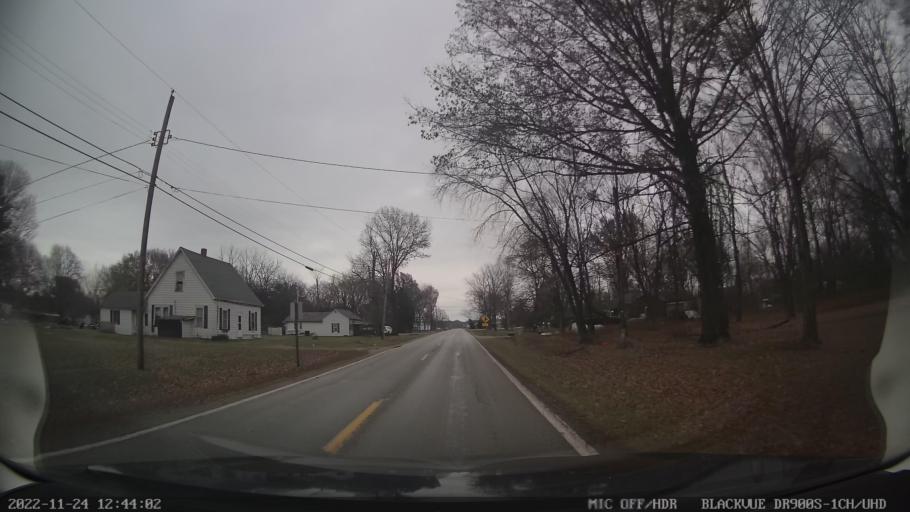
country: US
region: Illinois
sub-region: Macoupin County
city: Staunton
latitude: 38.9614
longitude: -89.7688
